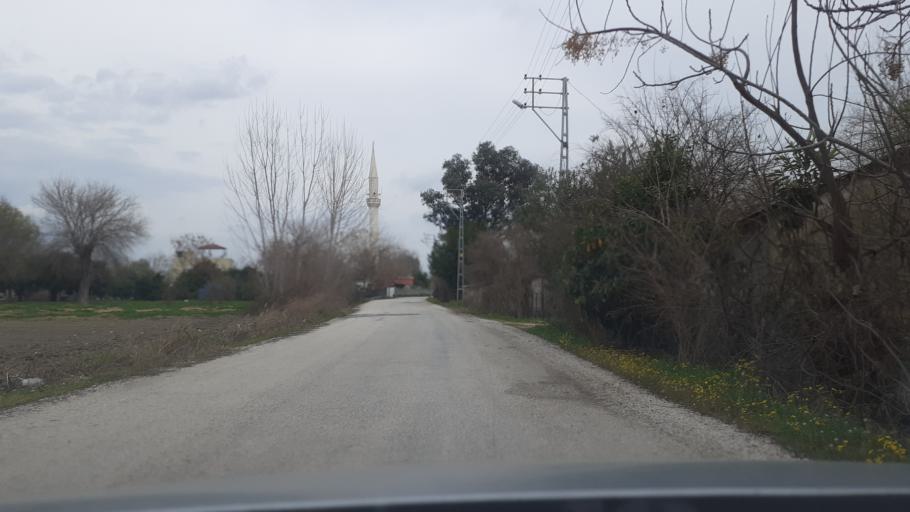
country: TR
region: Osmaniye
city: Sumbas
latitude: 37.3731
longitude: 35.9709
